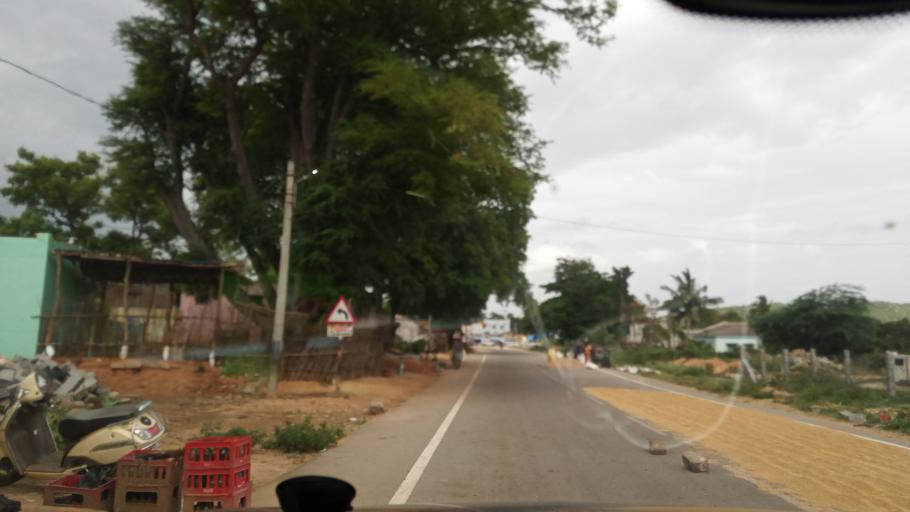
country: IN
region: Andhra Pradesh
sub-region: Chittoor
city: Palmaner
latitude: 13.1856
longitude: 78.8344
